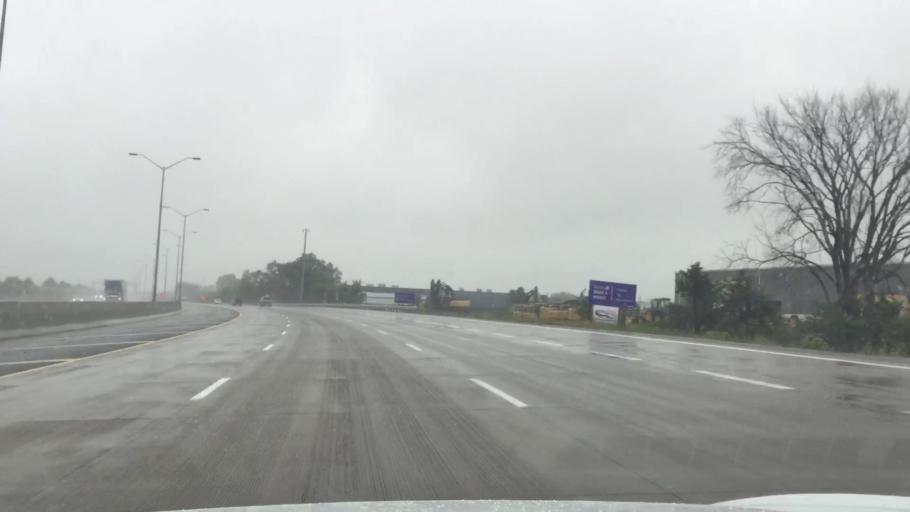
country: CA
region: Ontario
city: Windsor
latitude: 42.2341
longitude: -82.9856
